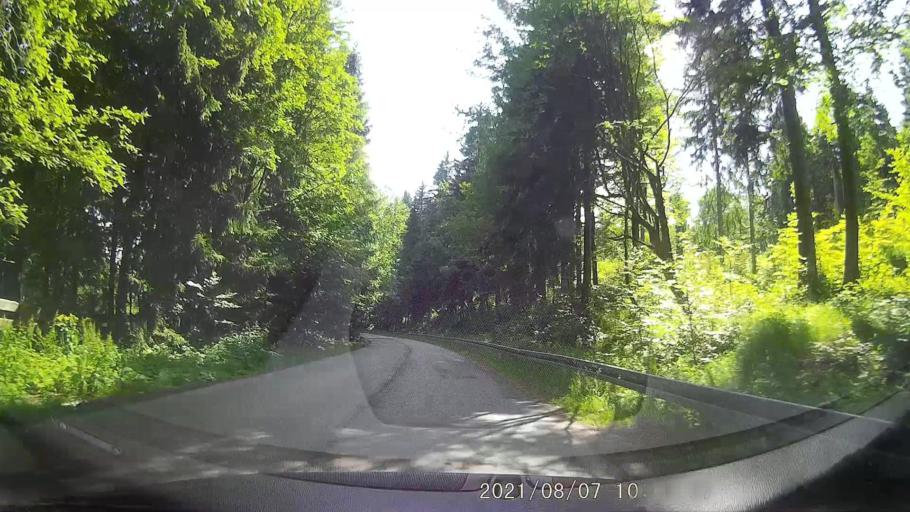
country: PL
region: Lower Silesian Voivodeship
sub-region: Powiat klodzki
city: Duszniki-Zdroj
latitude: 50.3272
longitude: 16.3985
